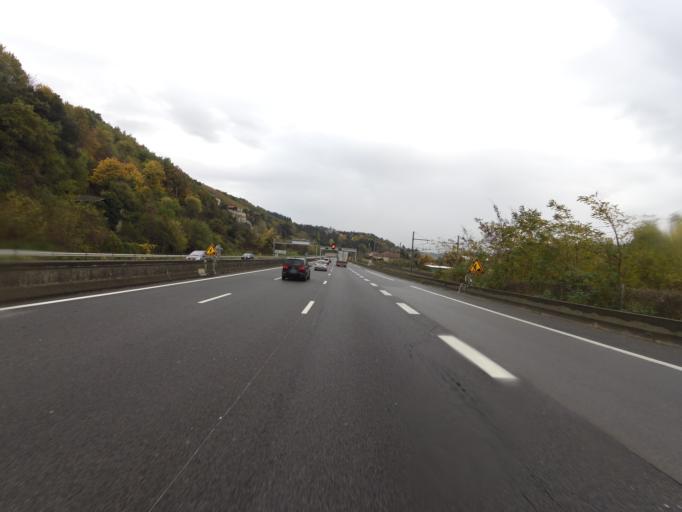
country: FR
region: Rhone-Alpes
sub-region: Departement du Rhone
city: Saint-Cyr-sur-le-Rhone
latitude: 45.5085
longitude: 4.8455
